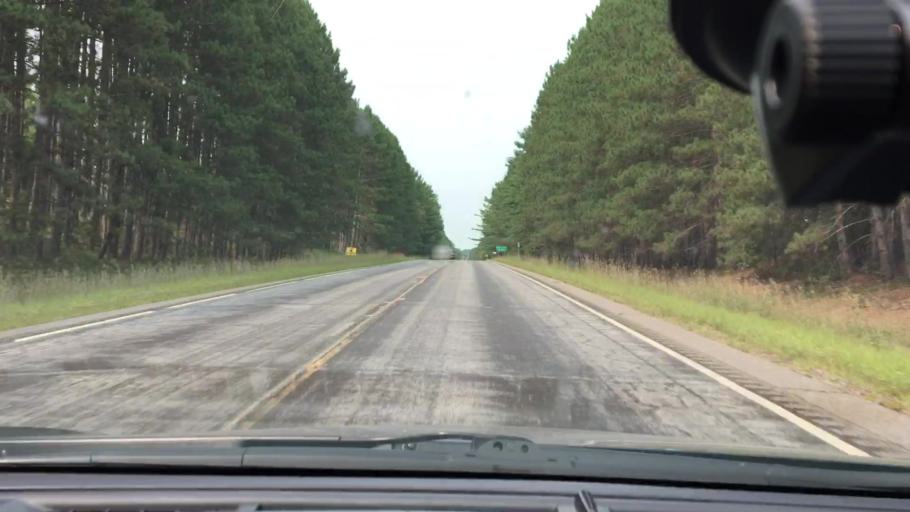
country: US
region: Minnesota
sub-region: Crow Wing County
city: Cross Lake
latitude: 46.7747
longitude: -93.9663
